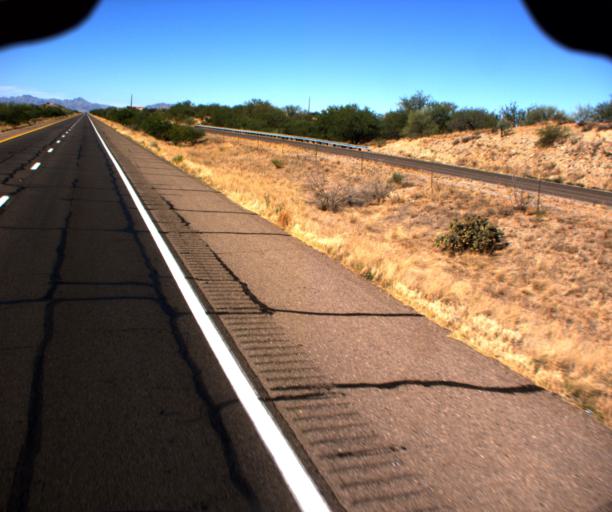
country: US
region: Arizona
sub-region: Pima County
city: Green Valley
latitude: 31.8180
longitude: -111.0071
